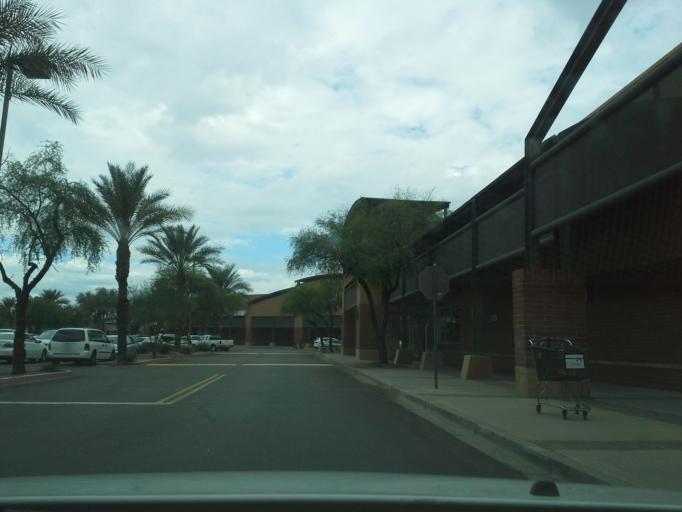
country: US
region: Arizona
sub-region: Maricopa County
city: Paradise Valley
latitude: 33.5847
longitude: -111.9756
